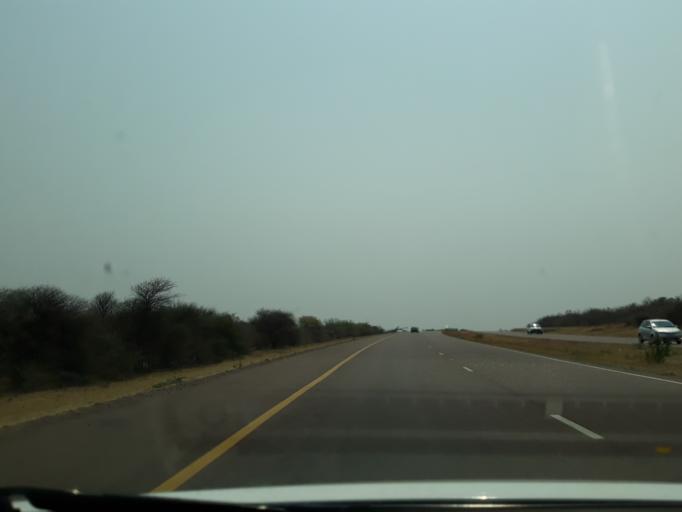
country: BW
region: Kgatleng
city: Bokaa
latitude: -24.4200
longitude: 26.0476
